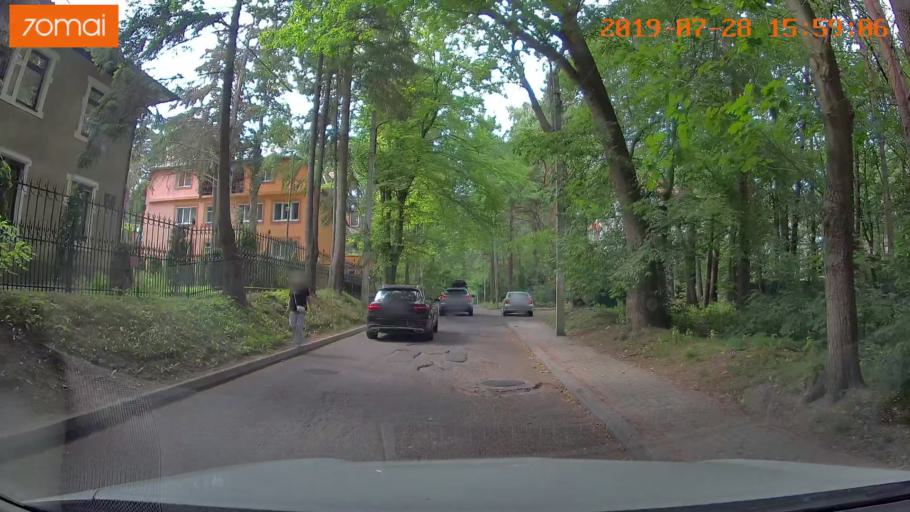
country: RU
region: Kaliningrad
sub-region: Gorod Svetlogorsk
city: Svetlogorsk
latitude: 54.9414
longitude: 20.1615
